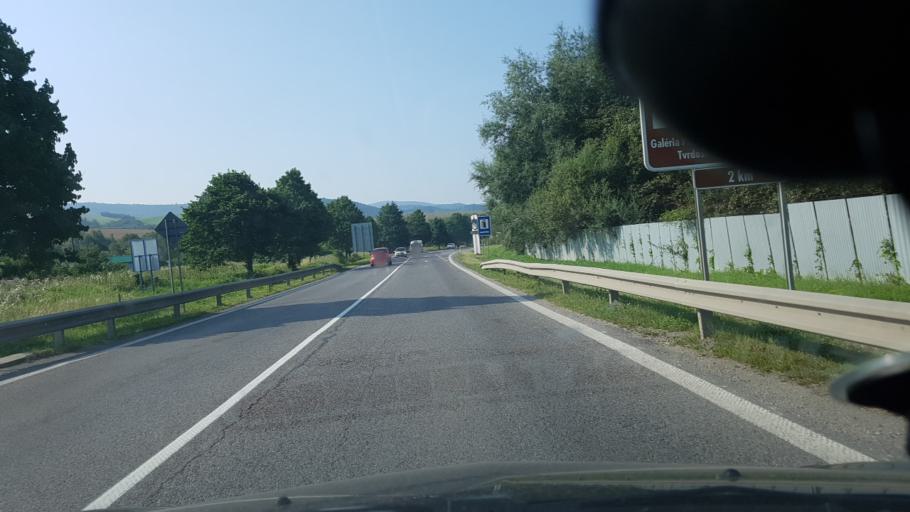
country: SK
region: Zilinsky
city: Tvrdosin
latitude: 49.3416
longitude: 19.5675
